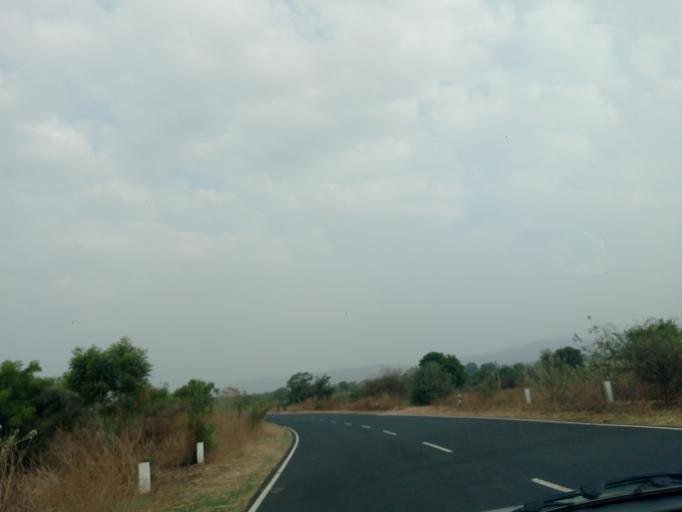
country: IN
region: Andhra Pradesh
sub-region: Prakasam
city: Diguvametta
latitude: 15.3778
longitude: 78.8693
